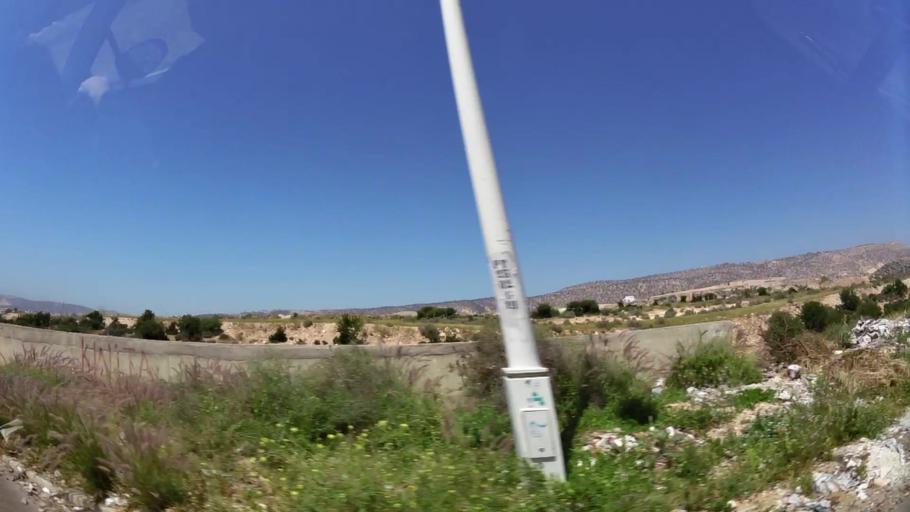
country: MA
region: Oued ed Dahab-Lagouira
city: Dakhla
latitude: 30.4384
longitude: -9.5677
